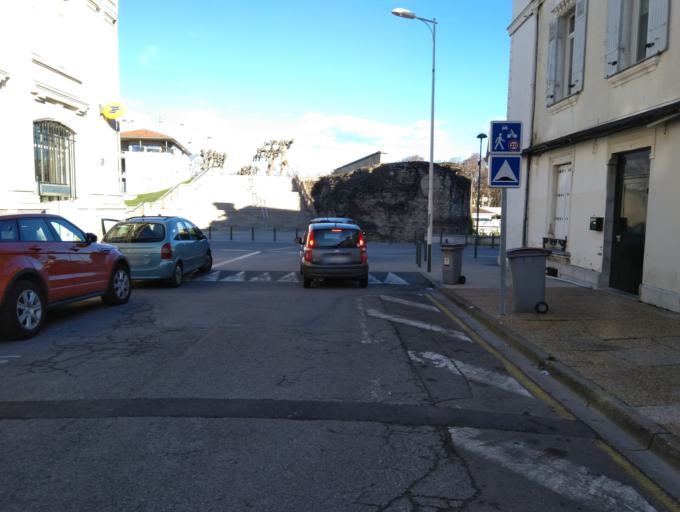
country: FR
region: Aquitaine
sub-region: Departement des Landes
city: Dax
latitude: 43.7104
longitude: -1.0506
